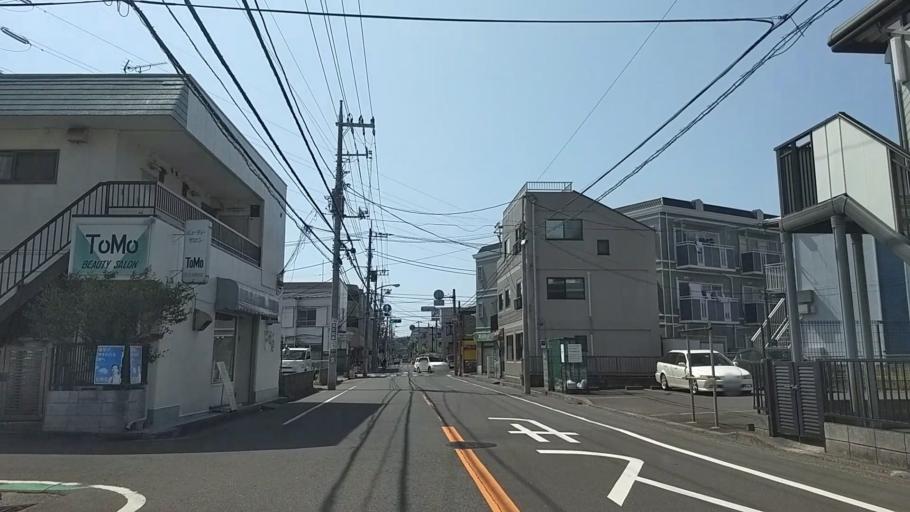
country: JP
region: Kanagawa
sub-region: Kawasaki-shi
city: Kawasaki
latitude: 35.5471
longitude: 139.6403
